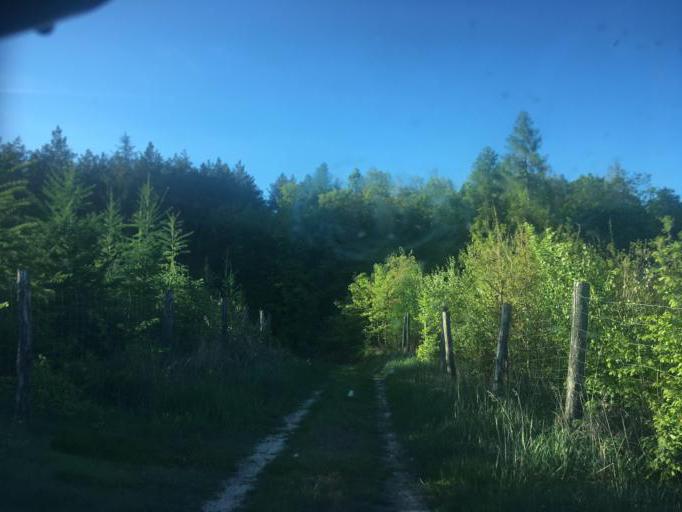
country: PL
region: Kujawsko-Pomorskie
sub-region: Powiat brodnicki
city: Gorzno
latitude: 53.2189
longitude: 19.7210
